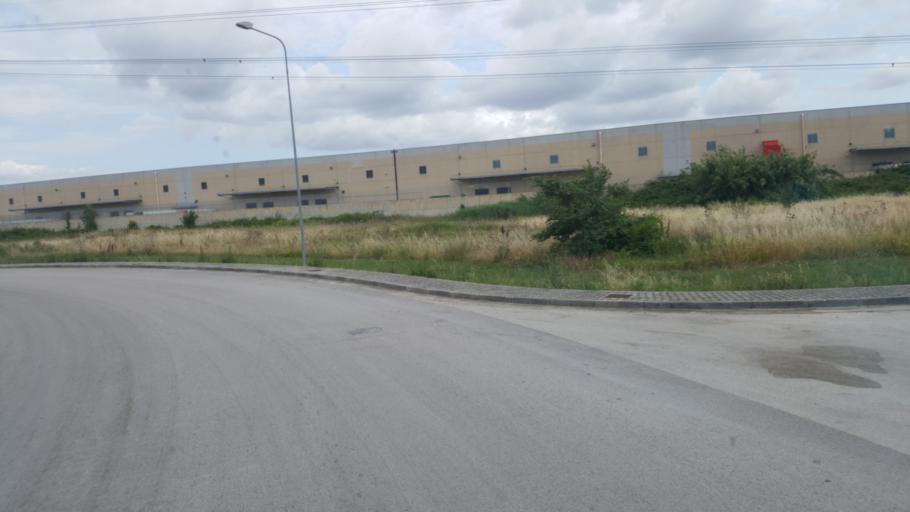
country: IT
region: Campania
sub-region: Provincia di Caserta
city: San Marco Evangelista
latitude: 41.0079
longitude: 14.3545
